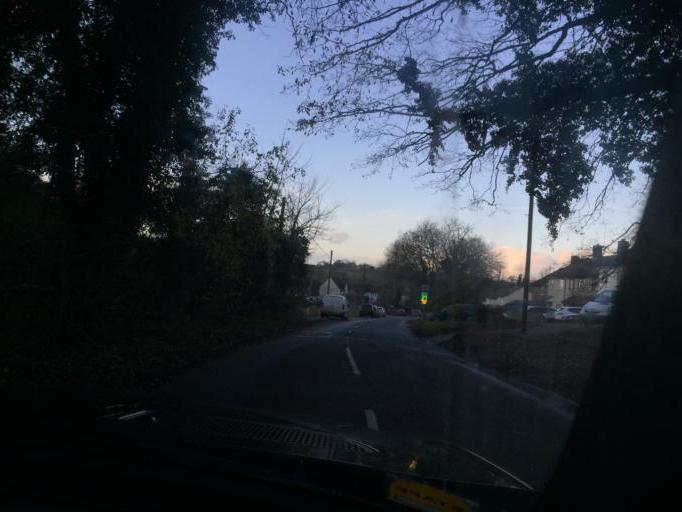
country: GB
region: England
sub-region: Northamptonshire
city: Brackley
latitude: 52.0853
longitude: -1.1458
